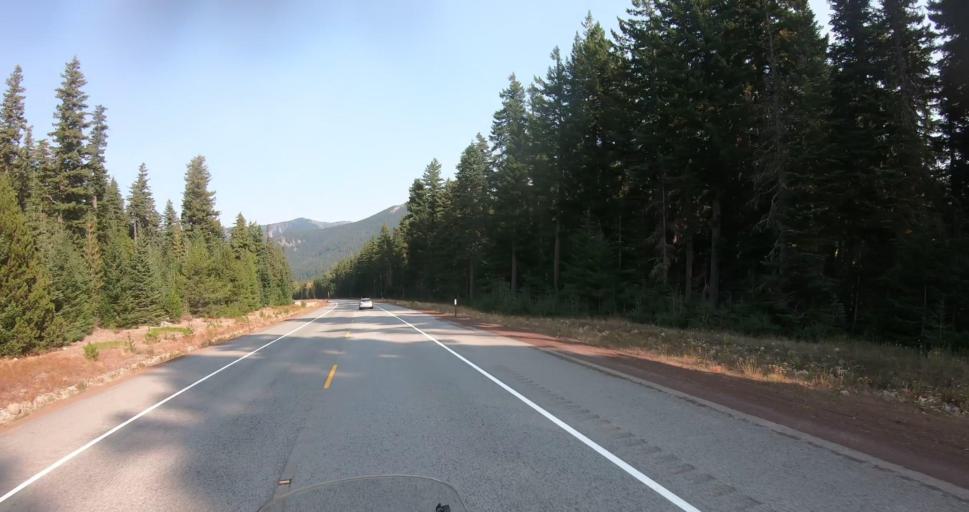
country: US
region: Oregon
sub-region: Hood River County
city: Odell
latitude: 45.3213
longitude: -121.6035
